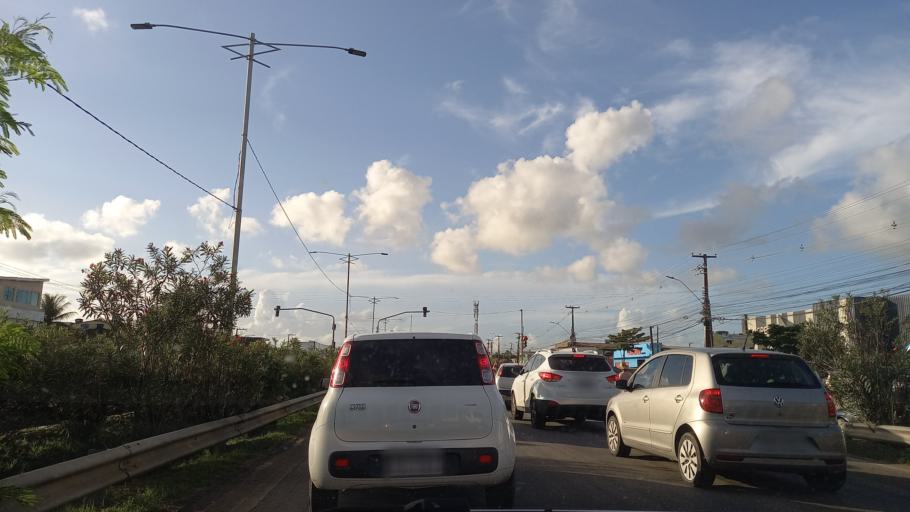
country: BR
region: Pernambuco
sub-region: Cabo De Santo Agostinho
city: Cabo
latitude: -8.2865
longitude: -35.0282
